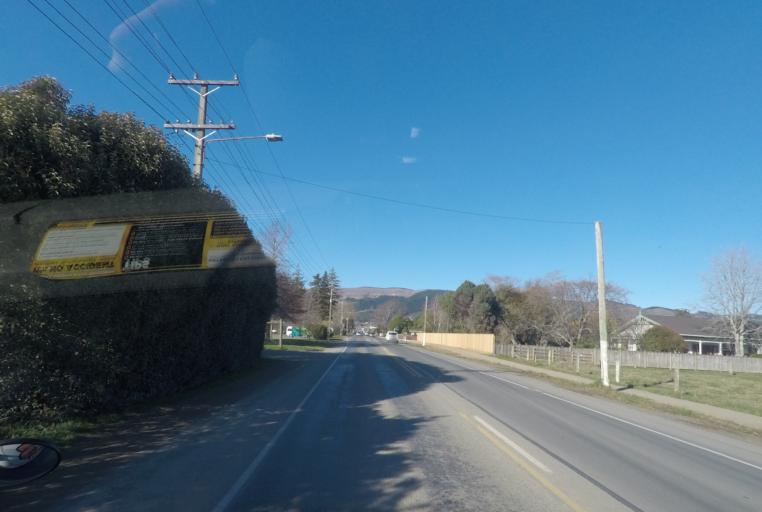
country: NZ
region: Tasman
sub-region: Tasman District
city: Richmond
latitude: -41.3311
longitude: 173.1757
